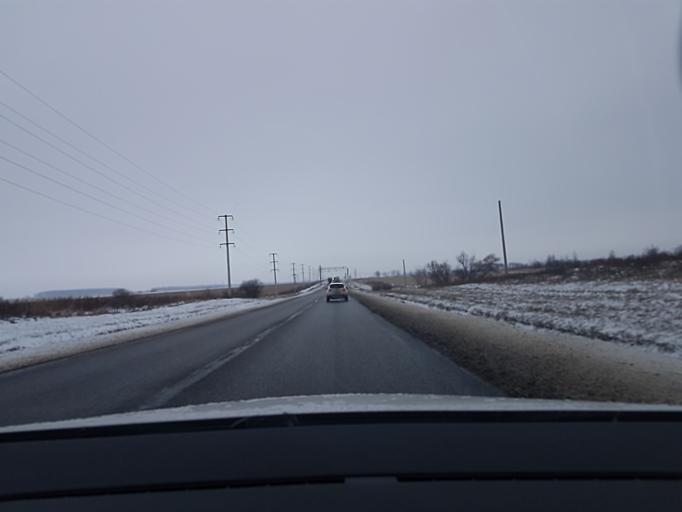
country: RU
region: Moskovskaya
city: Ozherel'ye
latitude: 54.7545
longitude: 38.2149
